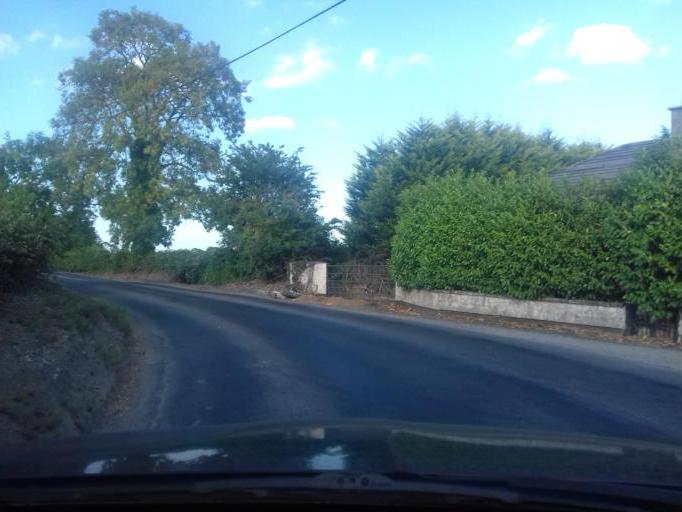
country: IE
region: Leinster
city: Hartstown
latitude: 53.4448
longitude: -6.4212
